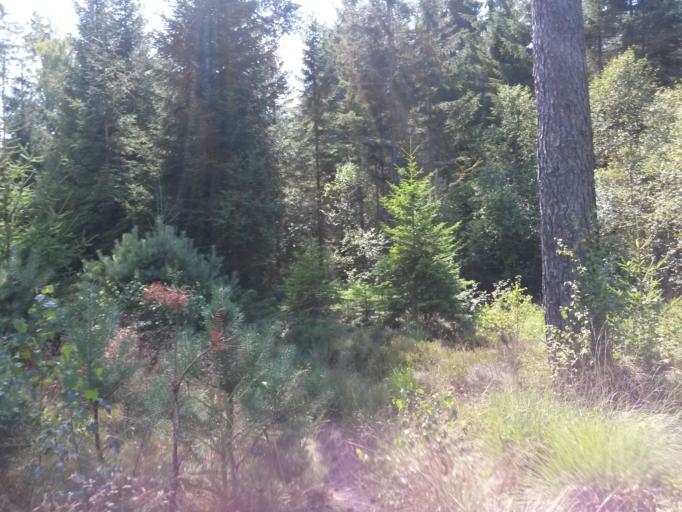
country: SE
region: Vaestra Goetaland
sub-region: Vargarda Kommun
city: Jonstorp
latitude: 57.9633
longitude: 12.6843
